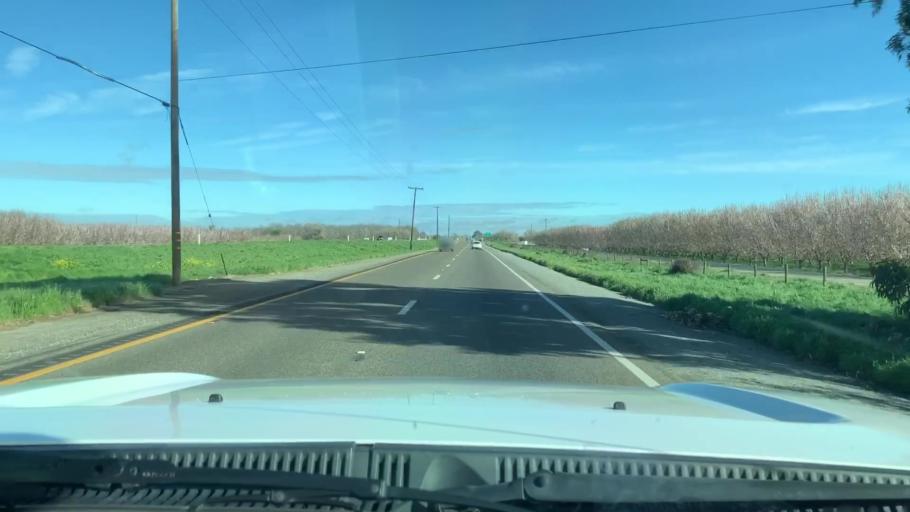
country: US
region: California
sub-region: Fresno County
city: Riverdale
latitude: 36.3821
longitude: -119.8095
